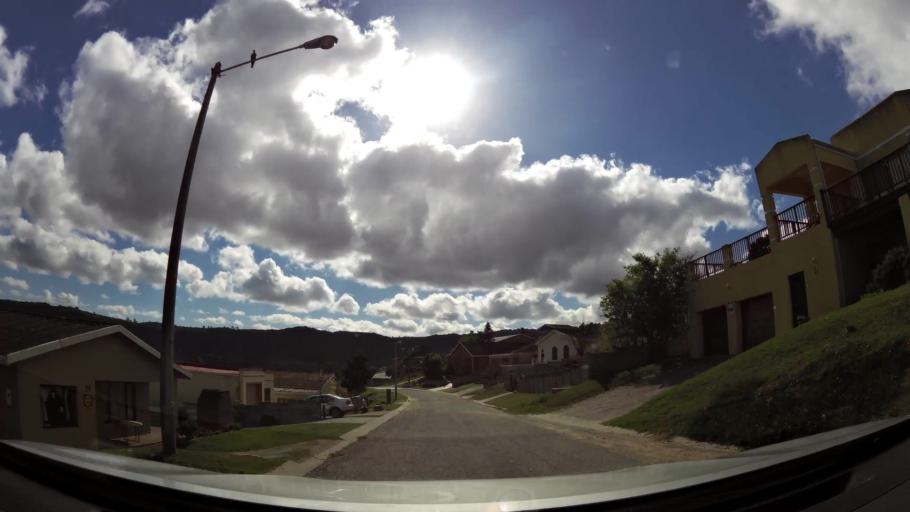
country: ZA
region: Western Cape
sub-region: Eden District Municipality
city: Knysna
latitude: -34.0501
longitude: 23.0824
